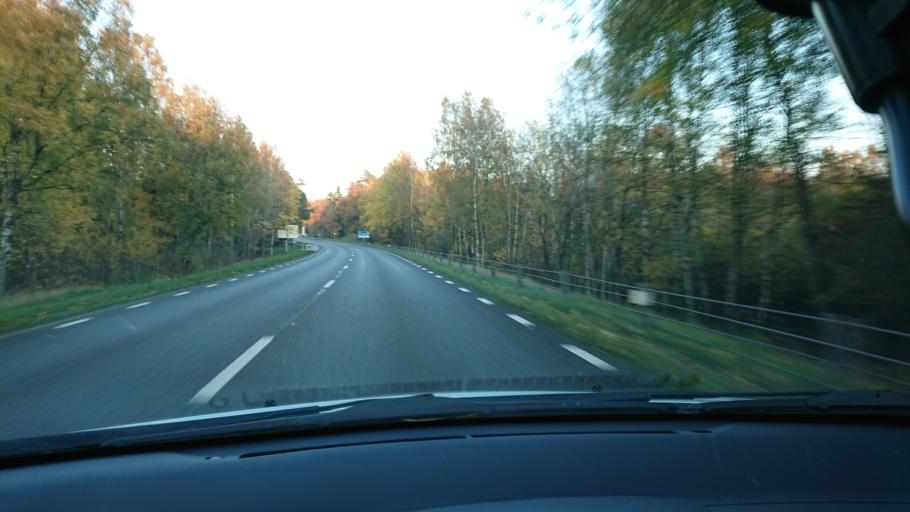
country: SE
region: Halland
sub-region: Halmstads Kommun
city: Oskarstrom
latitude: 56.7076
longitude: 13.0659
